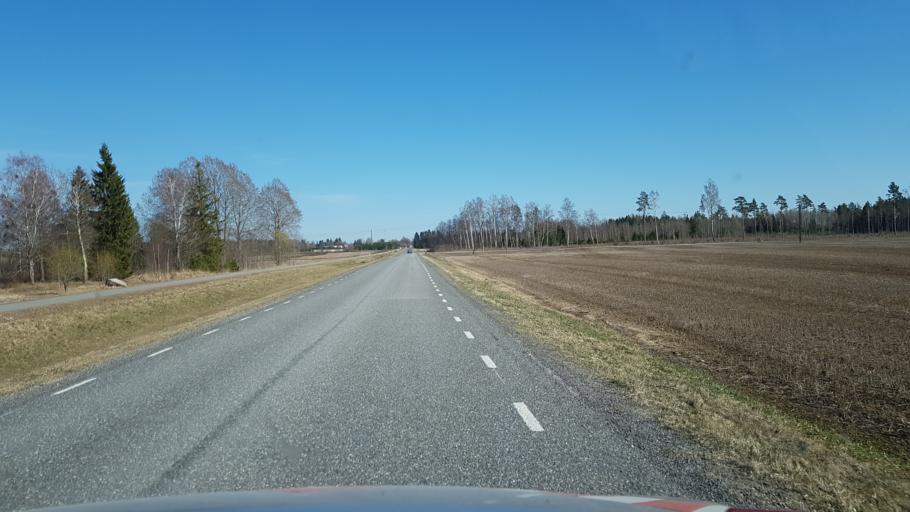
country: EE
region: Laeaene-Virumaa
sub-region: Rakke vald
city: Rakke
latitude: 58.9982
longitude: 26.2069
